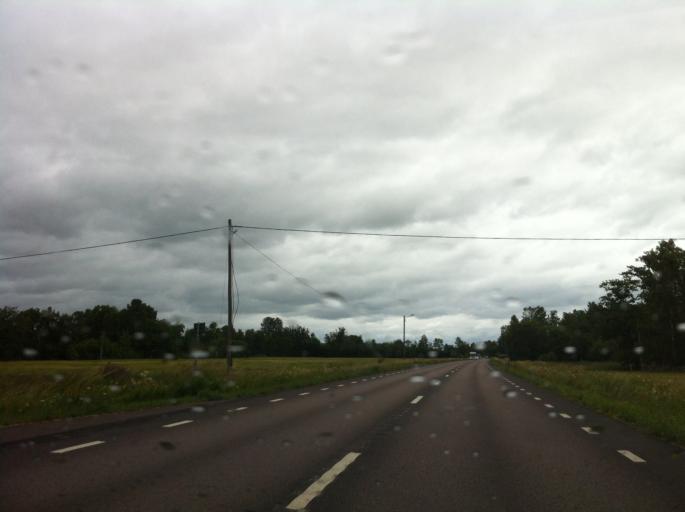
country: SE
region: Kalmar
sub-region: Borgholms Kommun
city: Borgholm
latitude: 57.1063
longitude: 16.9423
